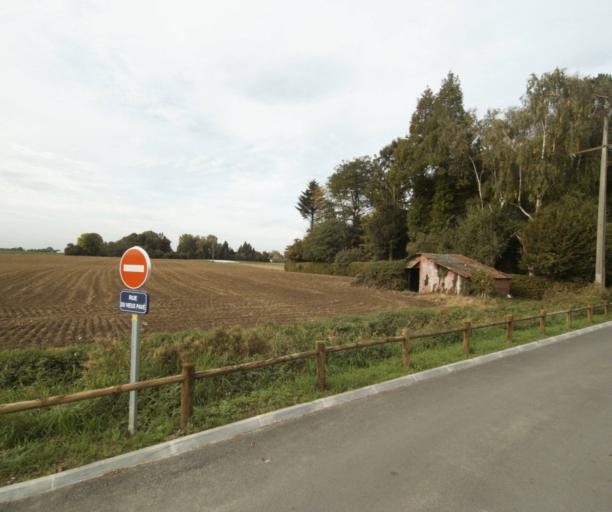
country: FR
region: Nord-Pas-de-Calais
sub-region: Departement du Nord
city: Radinghem-en-Weppes
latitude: 50.6124
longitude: 2.8858
